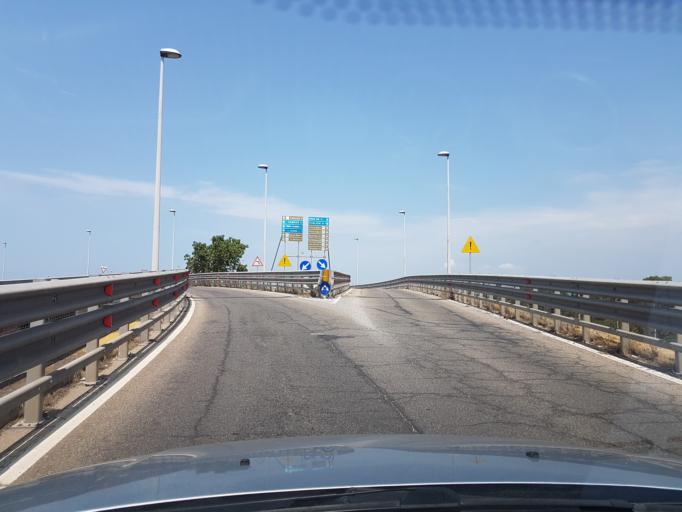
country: IT
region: Sardinia
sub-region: Provincia di Oristano
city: Donigala Fenugheddu
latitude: 39.9264
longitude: 8.5793
